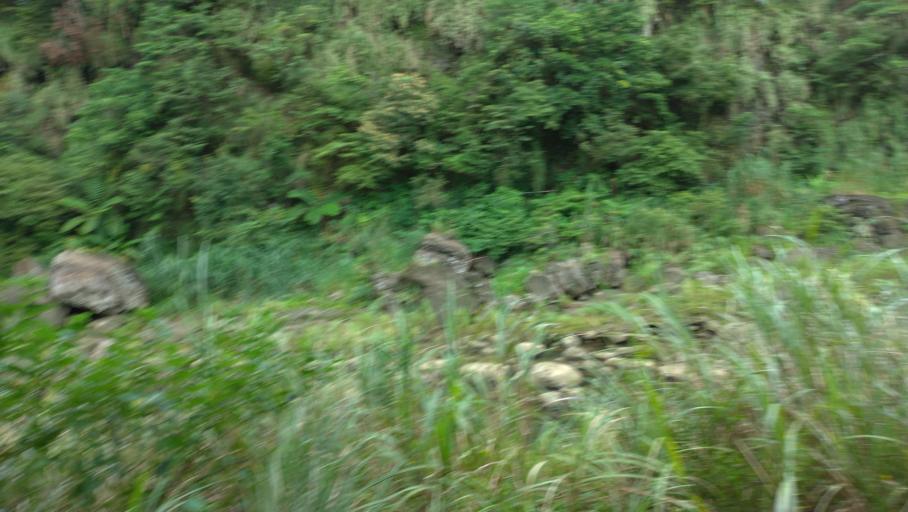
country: TW
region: Taiwan
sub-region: Keelung
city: Keelung
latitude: 25.0477
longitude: 121.7848
